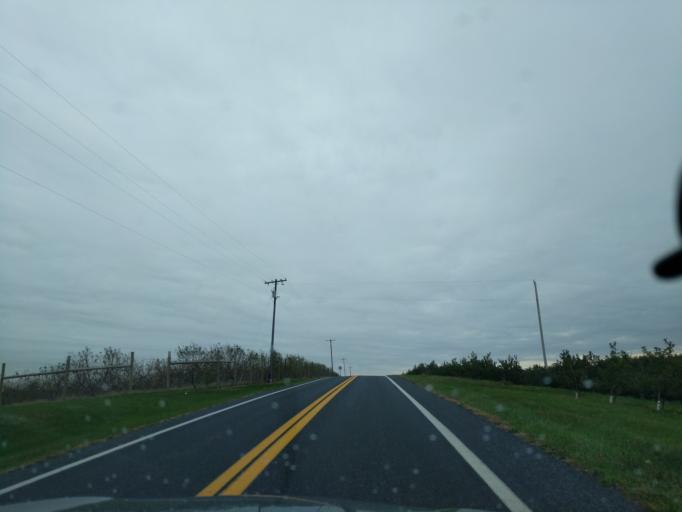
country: US
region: West Virginia
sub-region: Berkeley County
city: Martinsburg
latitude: 39.4442
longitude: -78.0296
